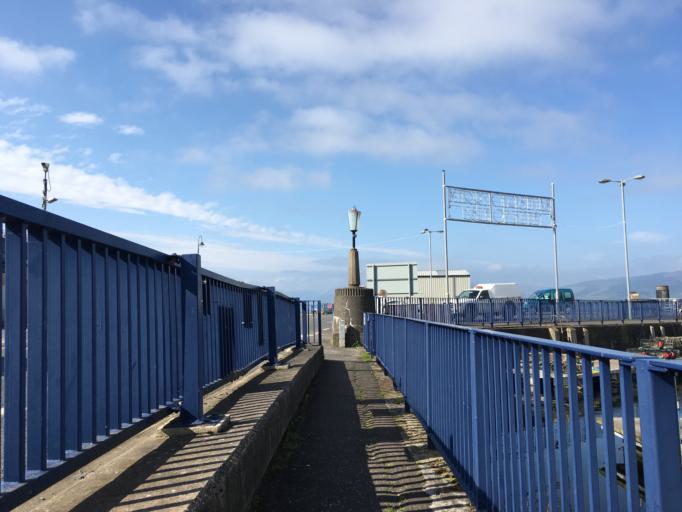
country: GB
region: Scotland
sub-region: Argyll and Bute
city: Rothesay
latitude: 55.8384
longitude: -5.0541
